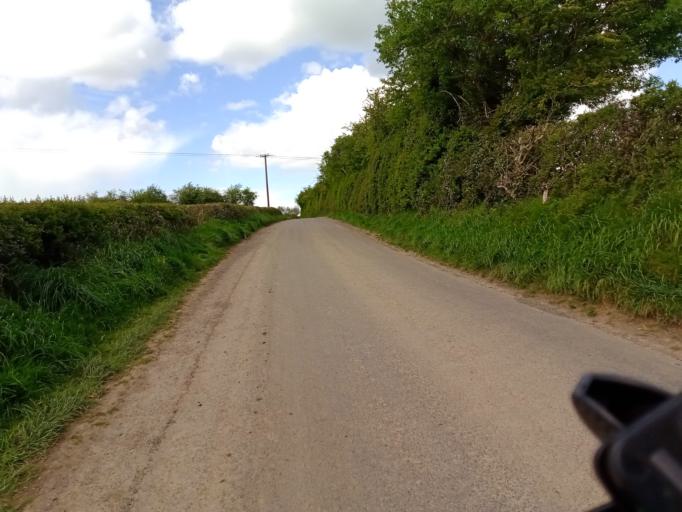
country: IE
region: Leinster
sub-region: Kilkenny
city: Thomastown
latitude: 52.5949
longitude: -7.1511
